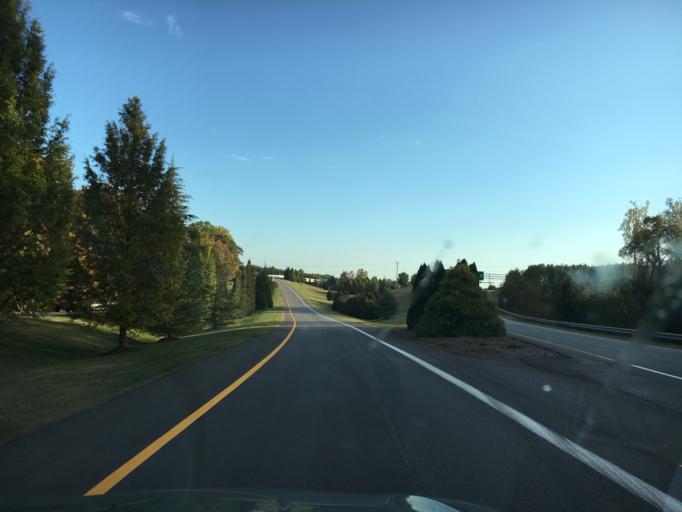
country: US
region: South Carolina
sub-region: Greenville County
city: Greer
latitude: 34.8819
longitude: -82.2155
